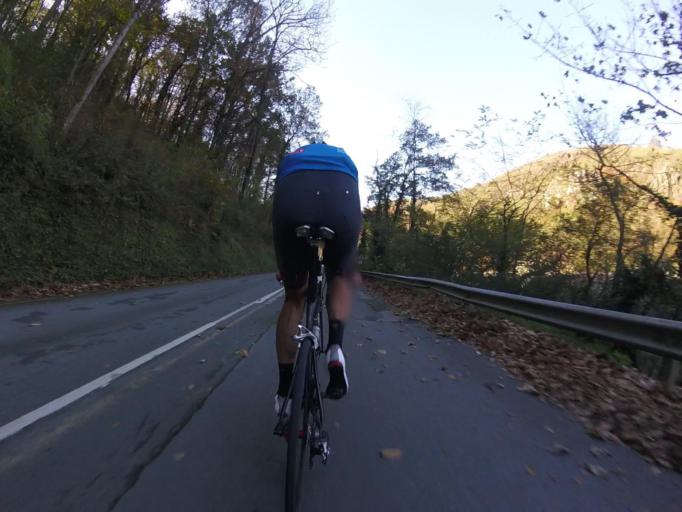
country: ES
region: Navarre
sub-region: Provincia de Navarra
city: Igantzi
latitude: 43.2369
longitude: -1.6744
